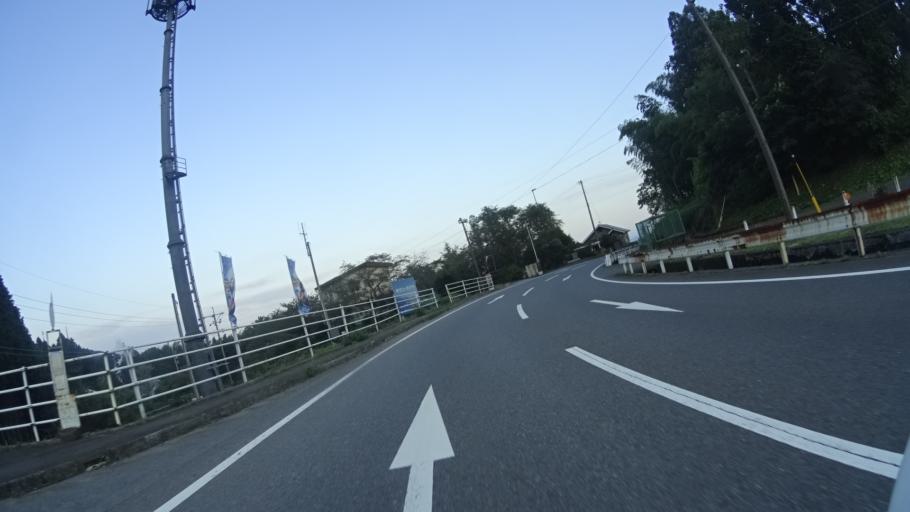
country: JP
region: Oita
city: Beppu
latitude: 33.3252
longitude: 131.4534
